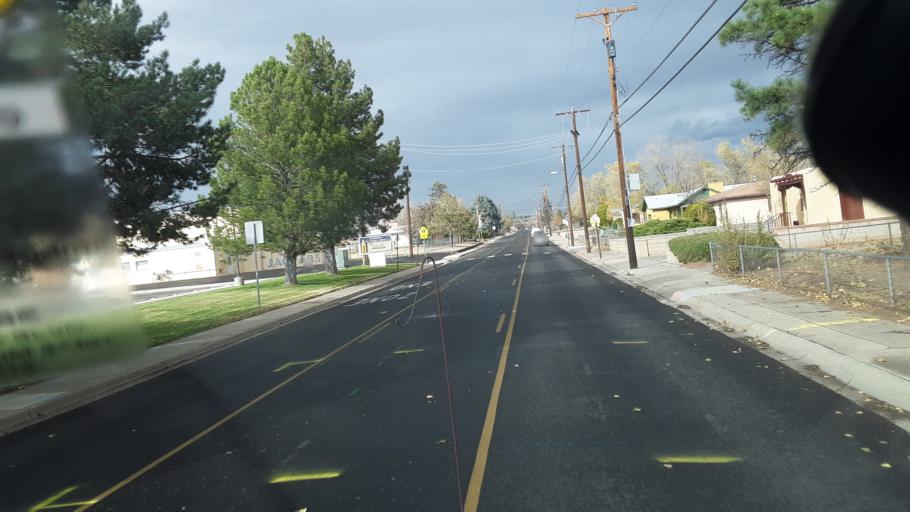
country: US
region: New Mexico
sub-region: San Juan County
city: Farmington
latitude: 36.7431
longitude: -108.1978
